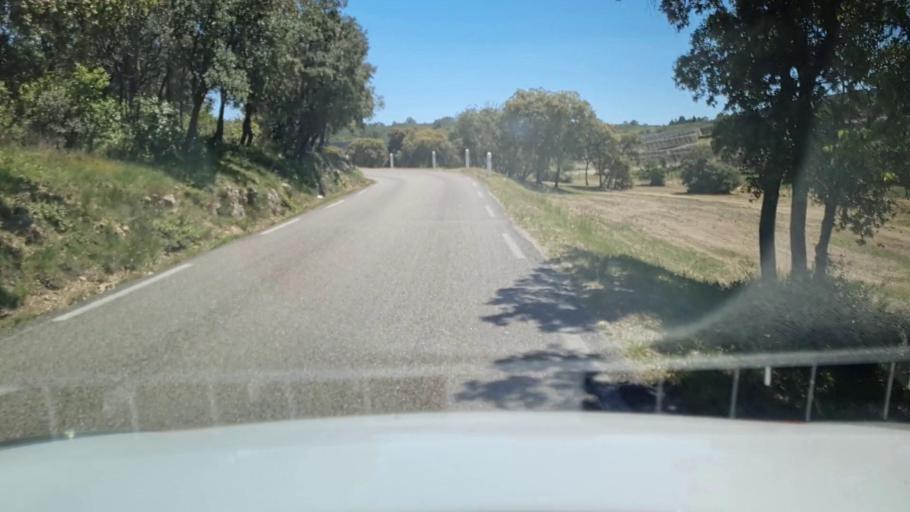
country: FR
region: Languedoc-Roussillon
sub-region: Departement du Gard
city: Clarensac
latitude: 43.8484
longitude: 4.2204
